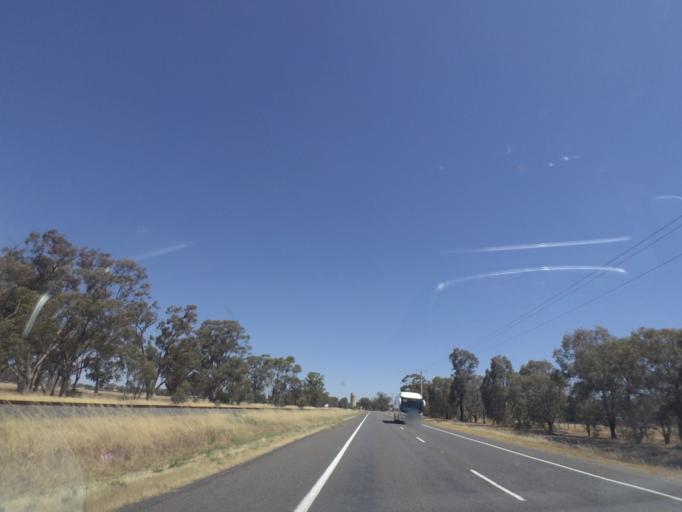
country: AU
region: Victoria
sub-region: Greater Shepparton
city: Shepparton
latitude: -36.2314
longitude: 145.4318
